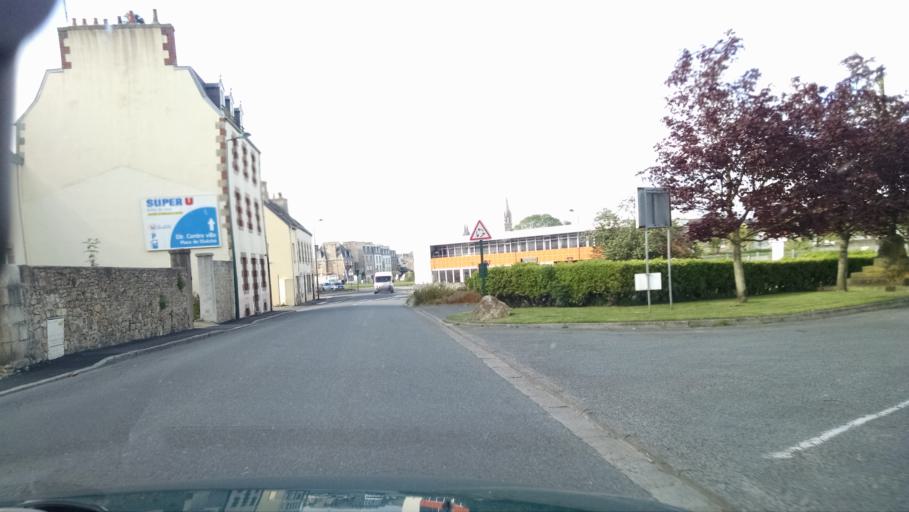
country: FR
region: Brittany
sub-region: Departement du Finistere
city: Saint-Pol-de-Leon
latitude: 48.6765
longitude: -3.9890
